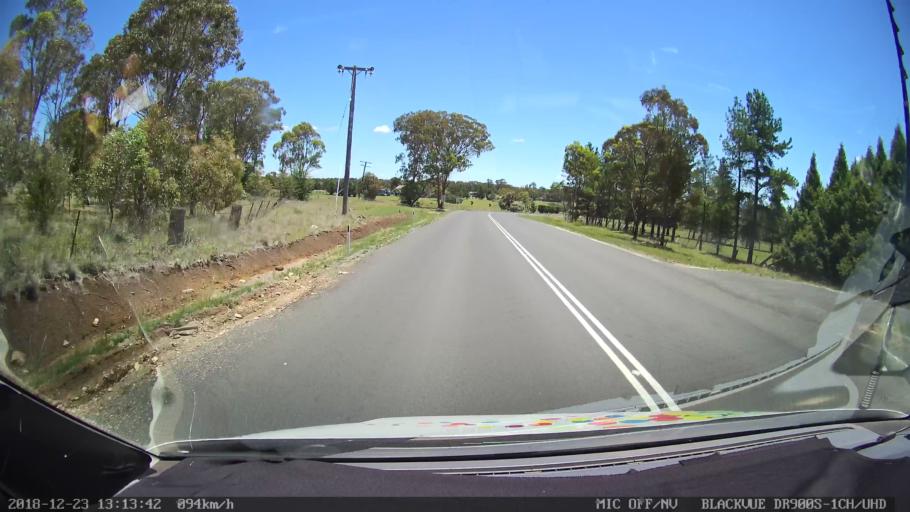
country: AU
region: New South Wales
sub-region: Armidale Dumaresq
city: Armidale
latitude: -30.5027
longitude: 151.5379
